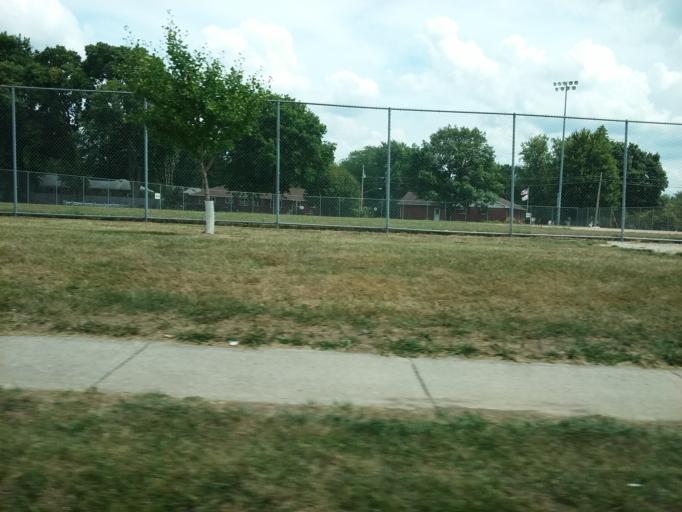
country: US
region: Ohio
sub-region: Hancock County
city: Findlay
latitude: 41.0465
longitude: -83.6330
